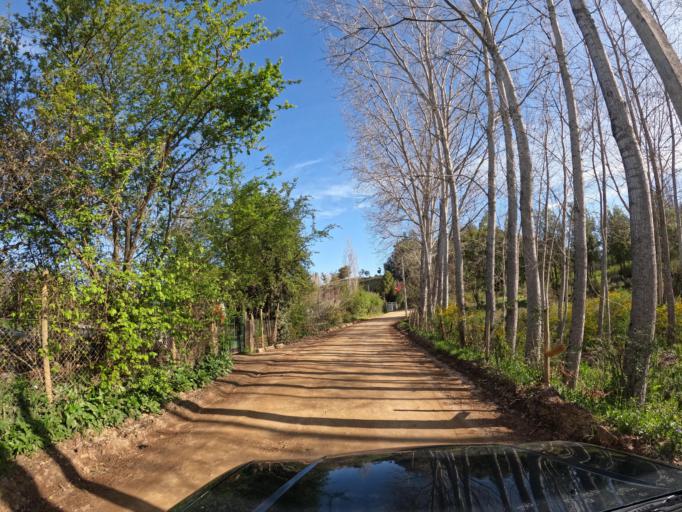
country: CL
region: Biobio
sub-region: Provincia de Biobio
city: La Laja
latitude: -37.1372
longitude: -72.7260
